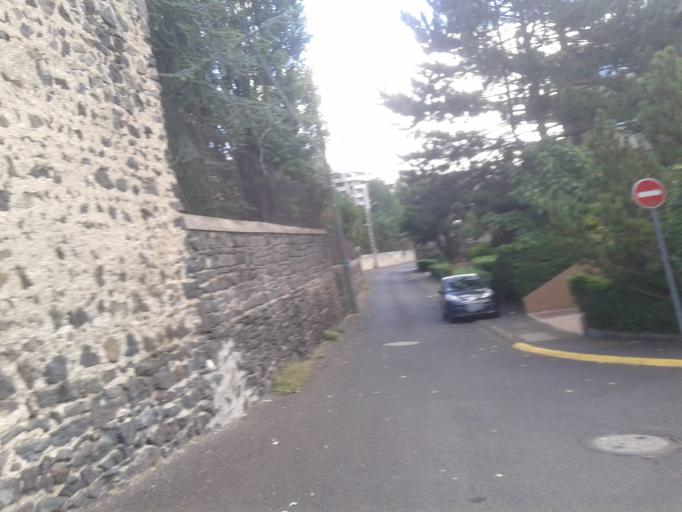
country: FR
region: Auvergne
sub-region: Departement du Puy-de-Dome
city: Chamalieres
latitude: 45.7749
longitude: 3.0593
